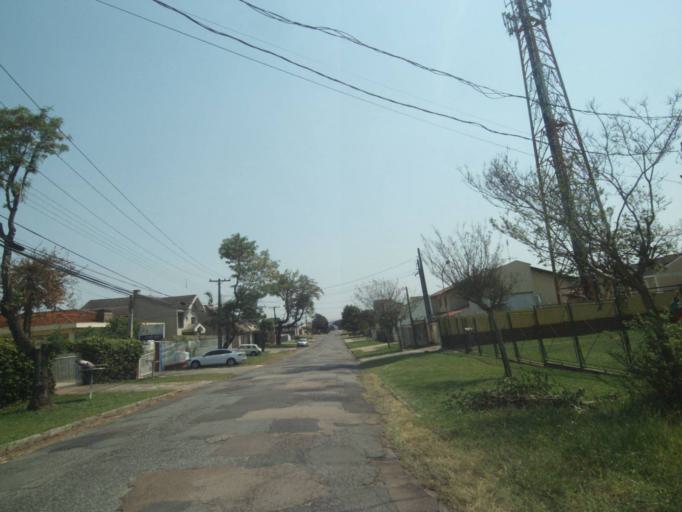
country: BR
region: Parana
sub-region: Sao Jose Dos Pinhais
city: Sao Jose dos Pinhais
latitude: -25.5111
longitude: -49.2615
